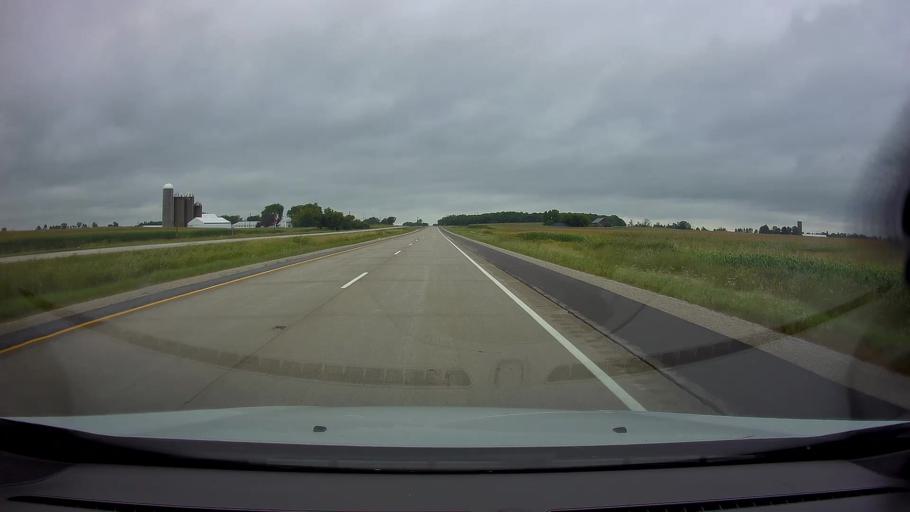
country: US
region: Wisconsin
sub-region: Brown County
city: Pulaski
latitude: 44.6227
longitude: -88.2710
